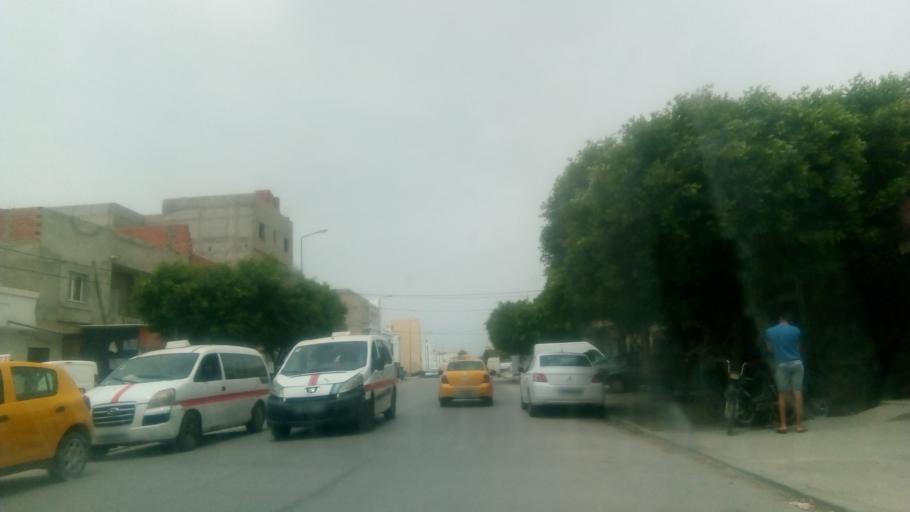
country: TN
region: Al Qayrawan
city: Kairouan
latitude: 35.6692
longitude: 10.0889
